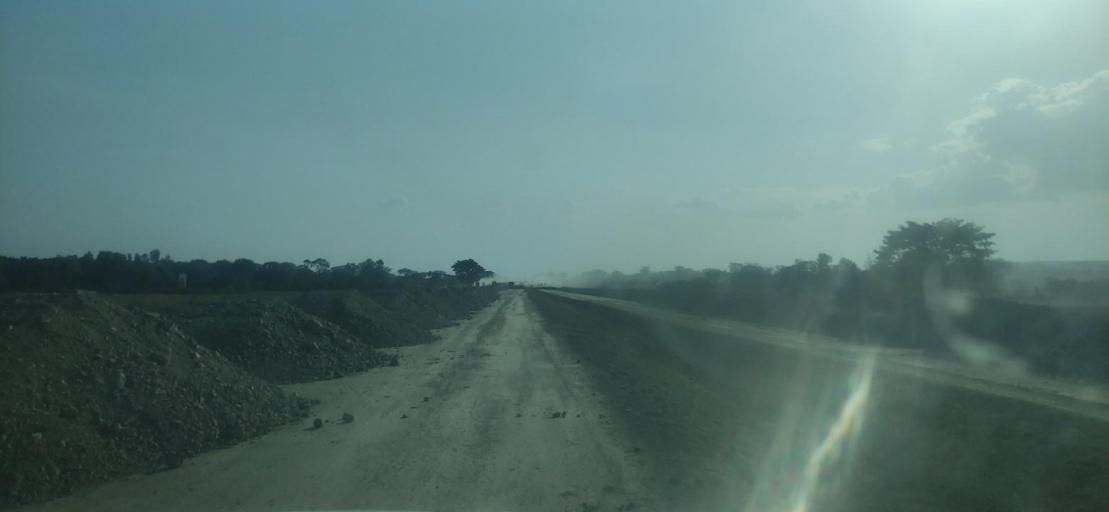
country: ET
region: Southern Nations, Nationalities, and People's Region
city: Hawassa
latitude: 7.1601
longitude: 38.4826
